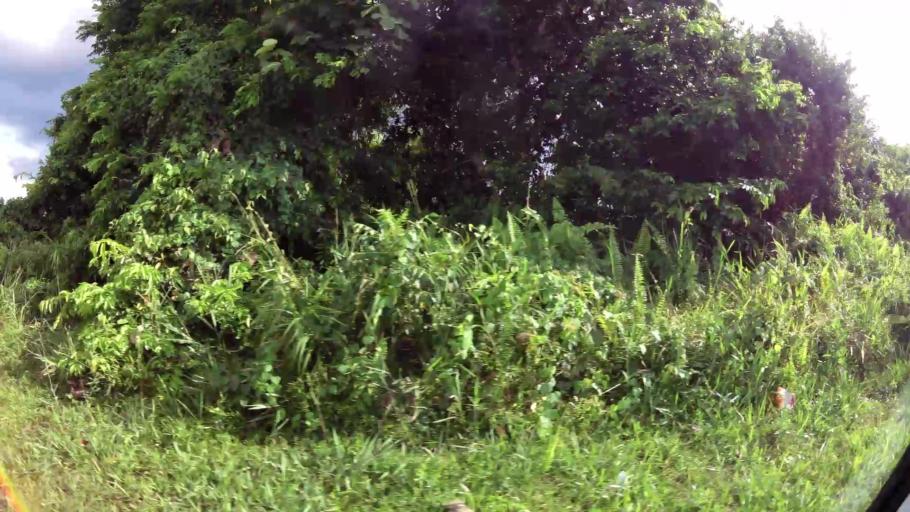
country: BN
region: Brunei and Muara
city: Bandar Seri Begawan
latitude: 4.9576
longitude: 114.9666
